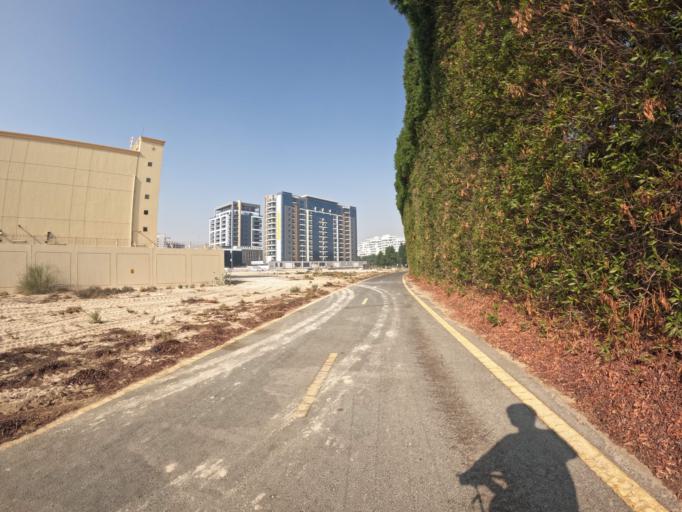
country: AE
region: Dubai
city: Dubai
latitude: 25.0964
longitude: 55.3197
